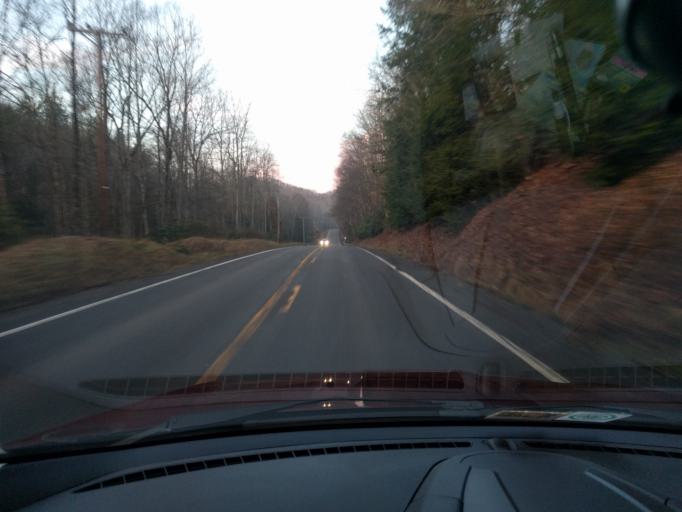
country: US
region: West Virginia
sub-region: Fayette County
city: Fayetteville
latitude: 38.0502
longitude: -80.9334
